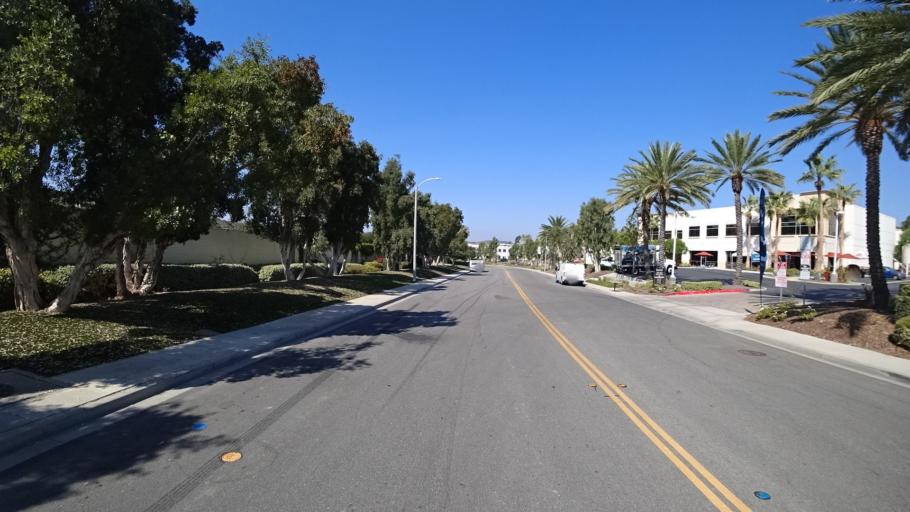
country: US
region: California
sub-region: Orange County
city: San Clemente
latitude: 33.4571
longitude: -117.5887
